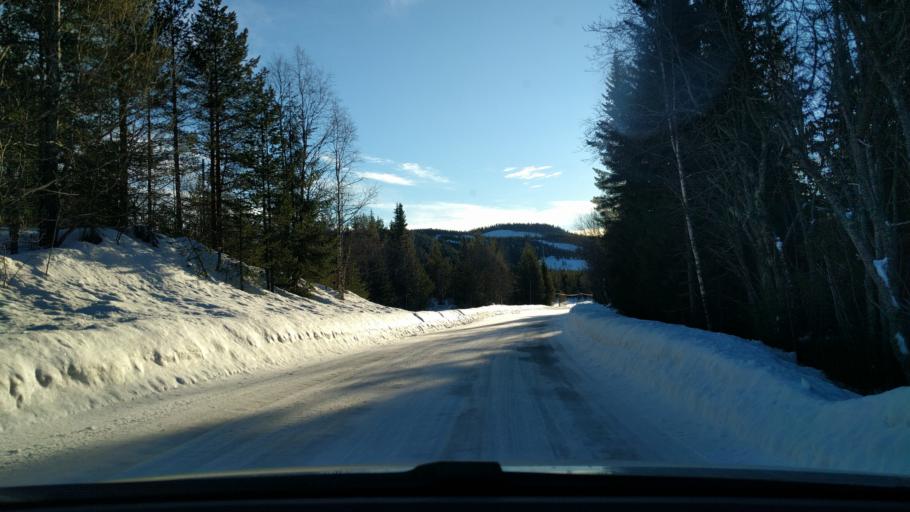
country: NO
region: Hedmark
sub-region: Trysil
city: Innbygda
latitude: 61.0961
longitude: 12.1660
